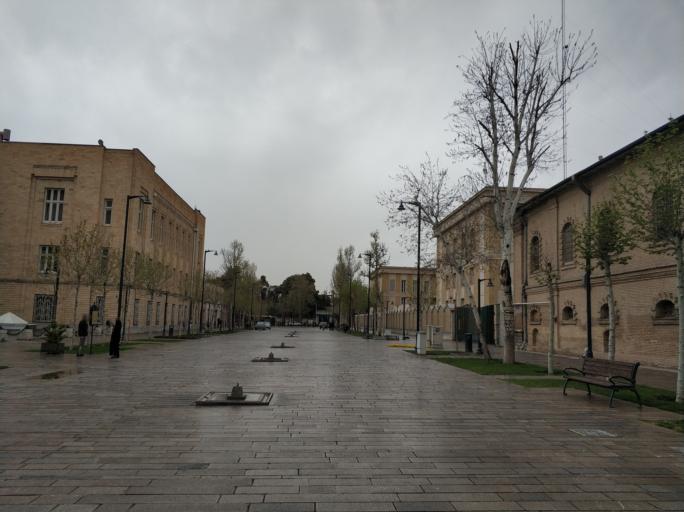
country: IR
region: Tehran
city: Tehran
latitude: 35.6887
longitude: 51.4162
